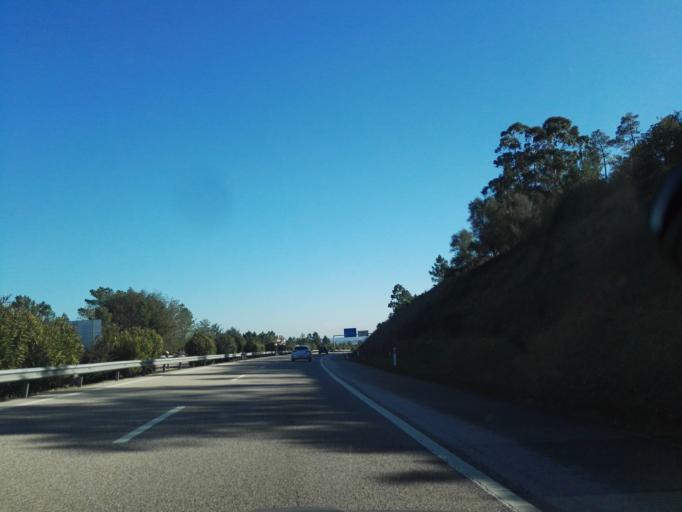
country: PT
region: Santarem
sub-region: Constancia
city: Constancia
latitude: 39.4855
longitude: -8.3602
